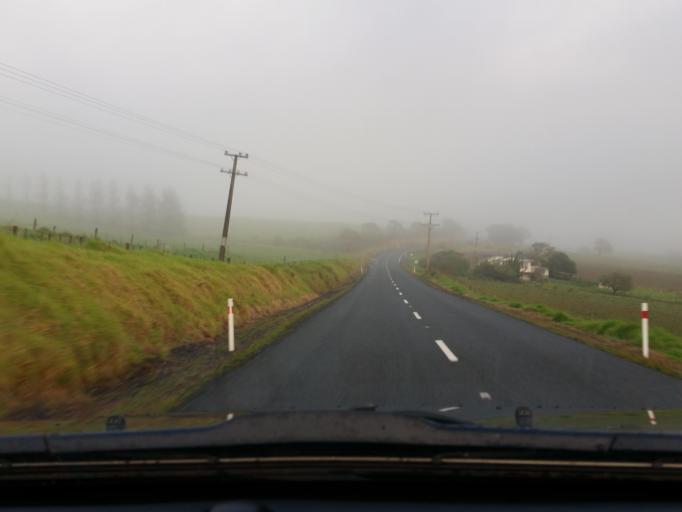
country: NZ
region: Northland
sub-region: Kaipara District
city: Dargaville
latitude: -35.9695
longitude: 173.9418
